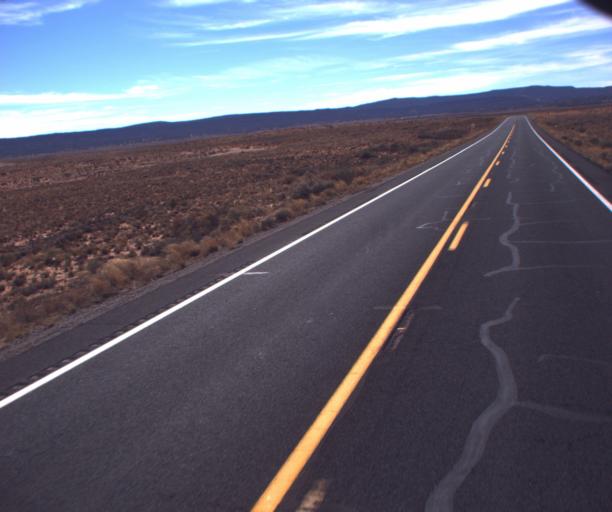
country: US
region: Arizona
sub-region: Coconino County
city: Kaibito
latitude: 36.4905
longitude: -110.7054
